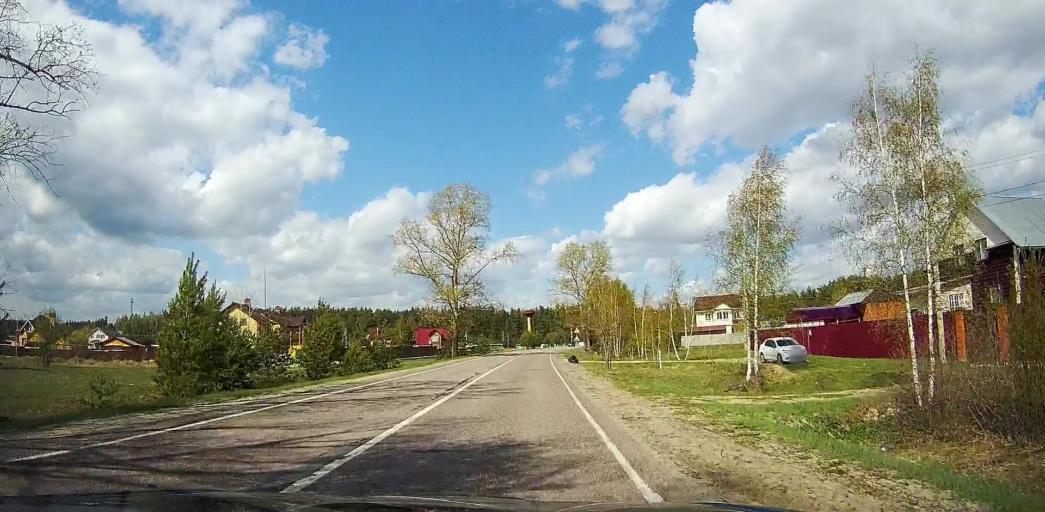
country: RU
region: Moskovskaya
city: Davydovo
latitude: 55.5600
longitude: 38.8131
